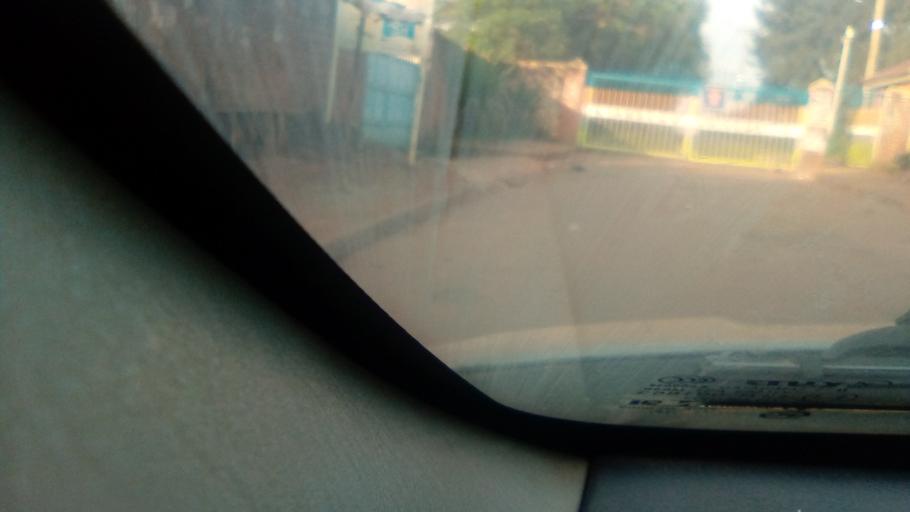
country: UG
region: Central Region
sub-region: Wakiso District
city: Kireka
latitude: 0.3457
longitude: 32.6344
